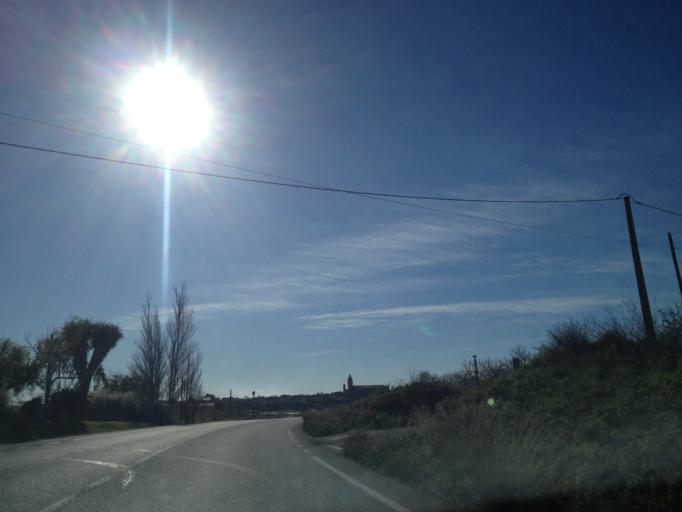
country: ES
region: Balearic Islands
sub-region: Illes Balears
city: Petra
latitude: 39.6243
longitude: 3.1095
